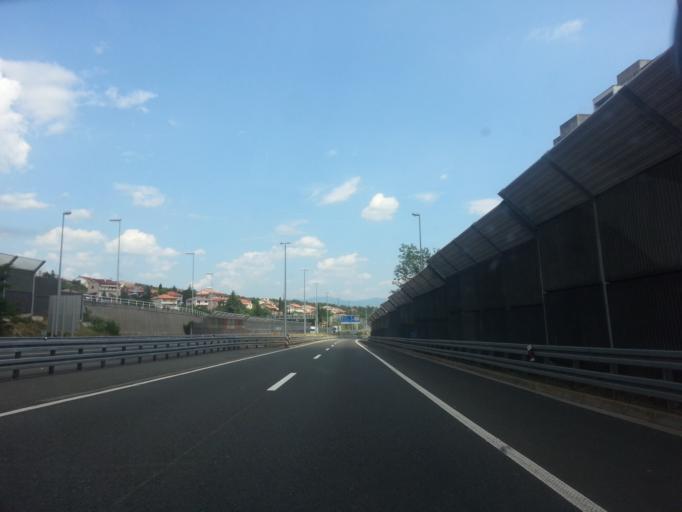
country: HR
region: Primorsko-Goranska
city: Marinici
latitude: 45.3473
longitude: 14.3861
